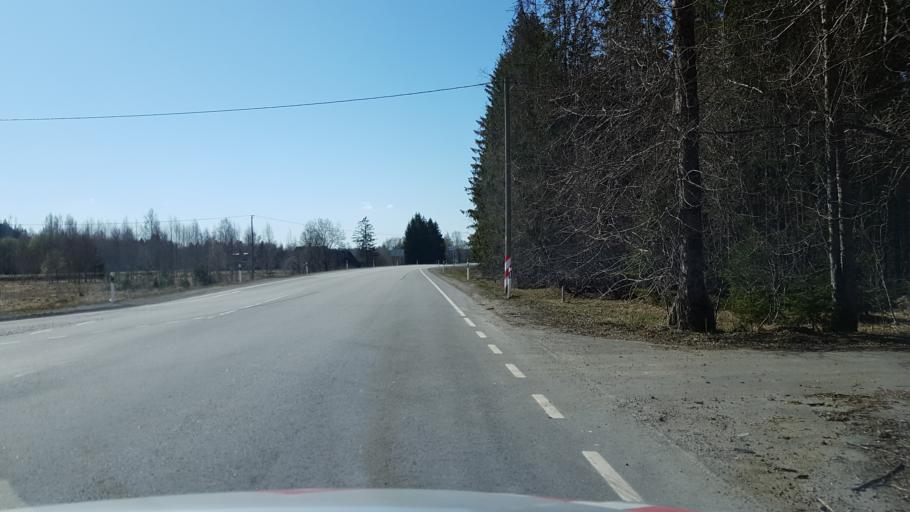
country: EE
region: Ida-Virumaa
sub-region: Kohtla-Jaerve linn
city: Kohtla-Jarve
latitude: 59.3277
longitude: 27.2643
